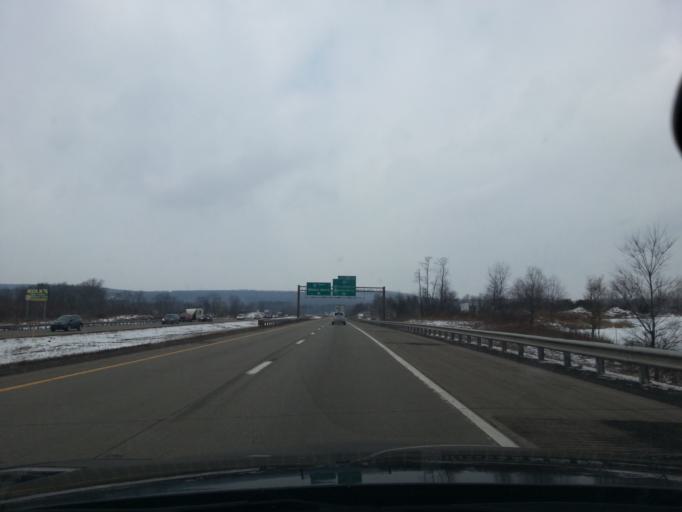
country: US
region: Pennsylvania
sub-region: Luzerne County
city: Conyngham
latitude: 41.0287
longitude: -76.0105
